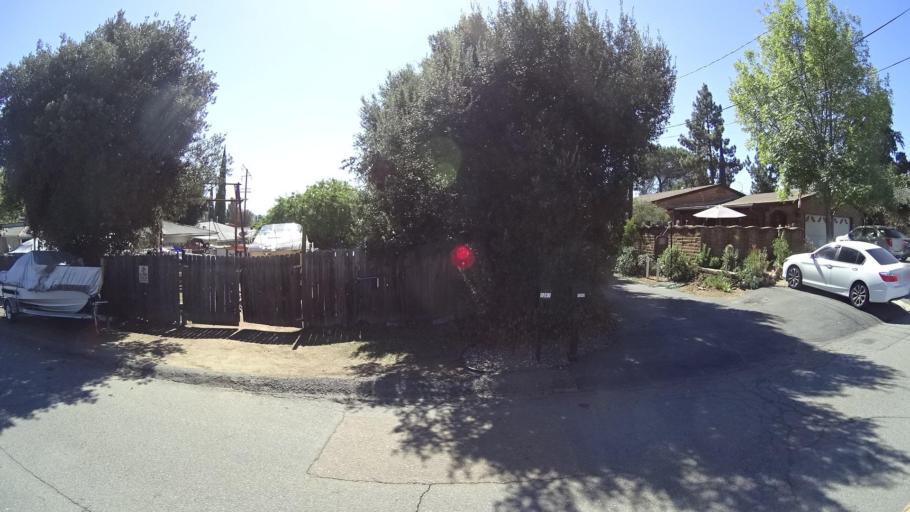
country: US
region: California
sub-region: San Diego County
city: Bostonia
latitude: 32.8188
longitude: -116.9363
